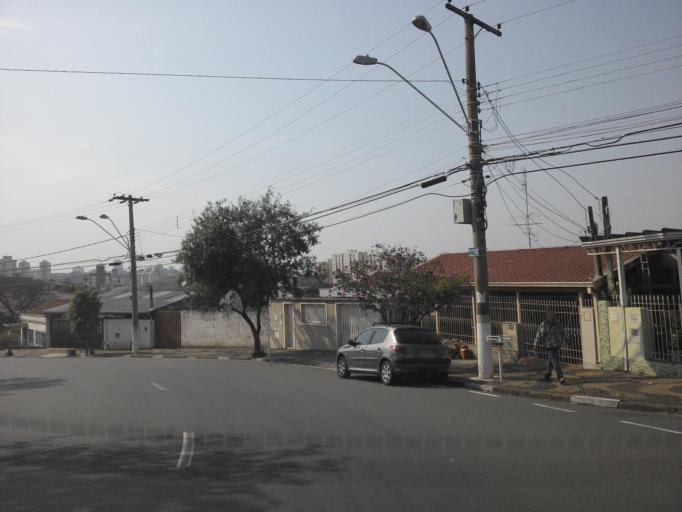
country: BR
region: Sao Paulo
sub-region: Campinas
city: Campinas
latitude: -22.9111
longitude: -47.0864
